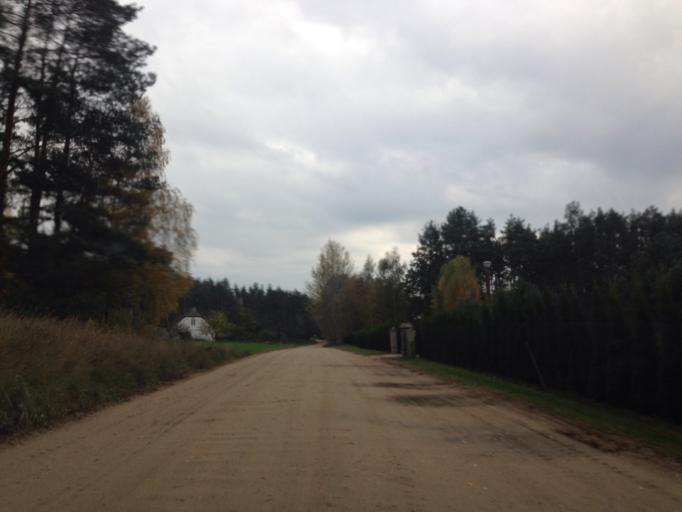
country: PL
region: Kujawsko-Pomorskie
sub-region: Powiat brodnicki
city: Brzozie
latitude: 53.3098
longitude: 19.5599
